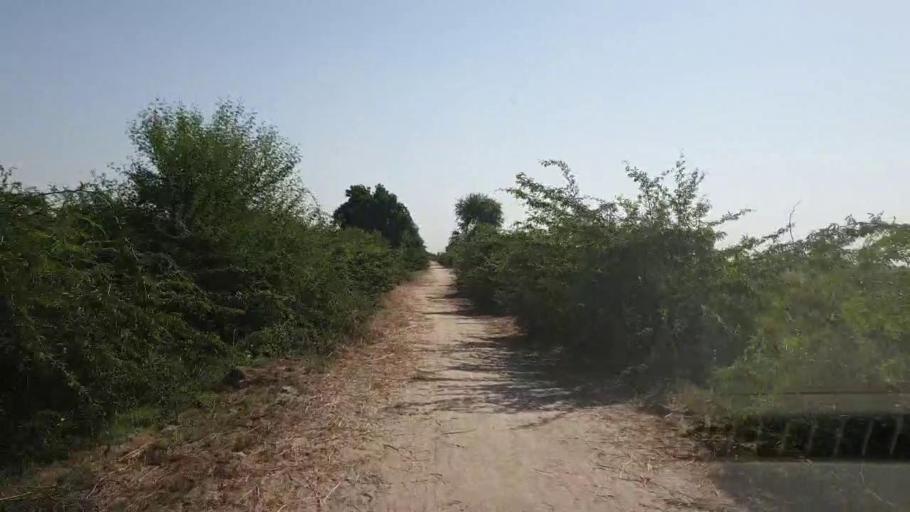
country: PK
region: Sindh
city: Kadhan
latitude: 24.6210
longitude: 68.9960
